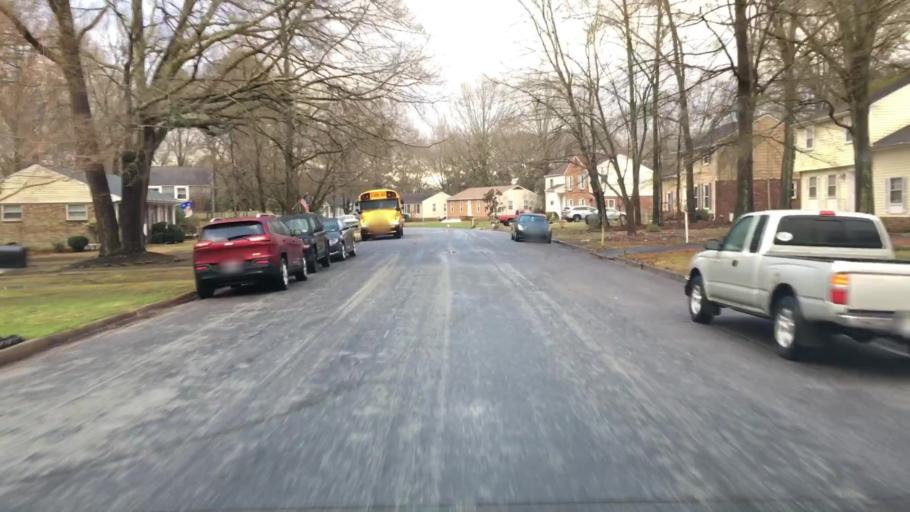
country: US
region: Virginia
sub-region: Chesterfield County
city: Bon Air
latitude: 37.5136
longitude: -77.6234
